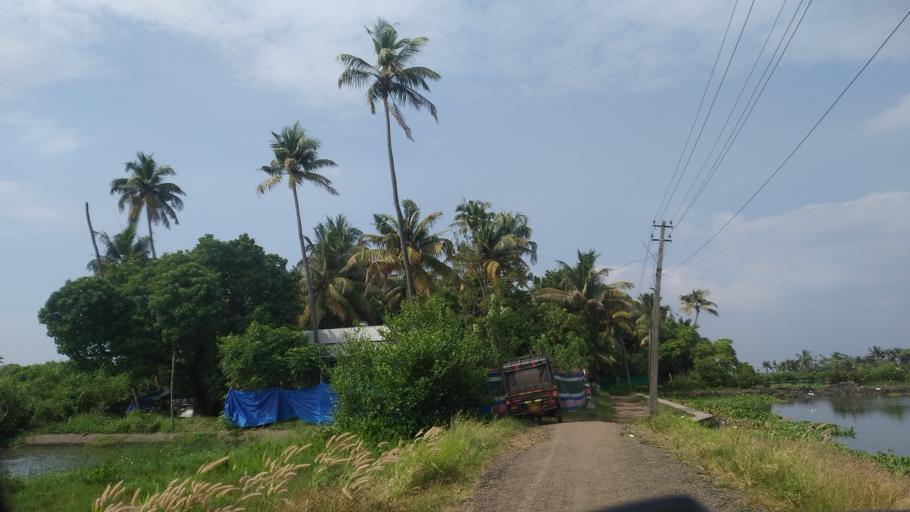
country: IN
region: Kerala
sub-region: Ernakulam
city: Elur
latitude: 10.0881
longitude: 76.2177
